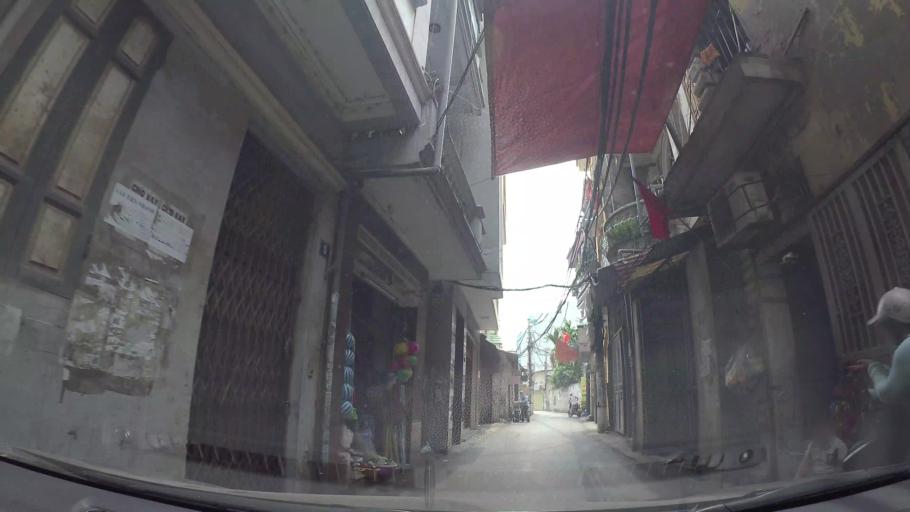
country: VN
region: Ha Noi
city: Van Dien
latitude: 20.9781
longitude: 105.8484
